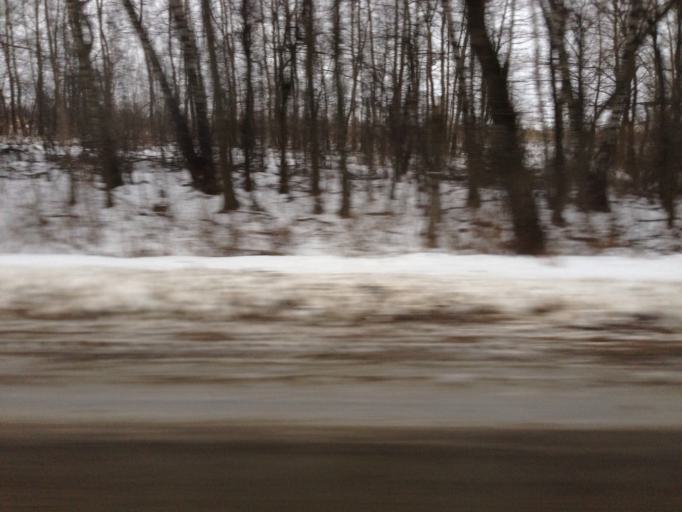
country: RU
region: Tula
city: Partizan
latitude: 54.0098
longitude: 38.0964
